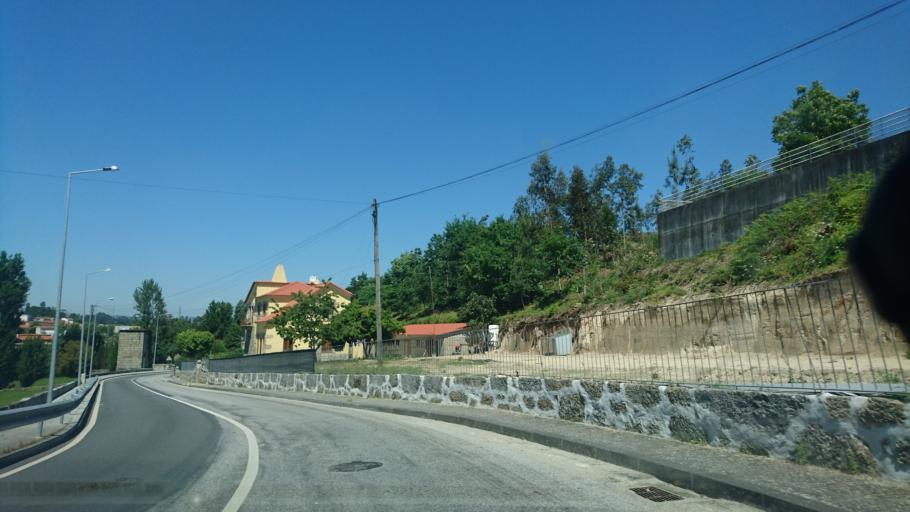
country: PT
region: Porto
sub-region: Paredes
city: Baltar
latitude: 41.1661
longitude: -8.3517
